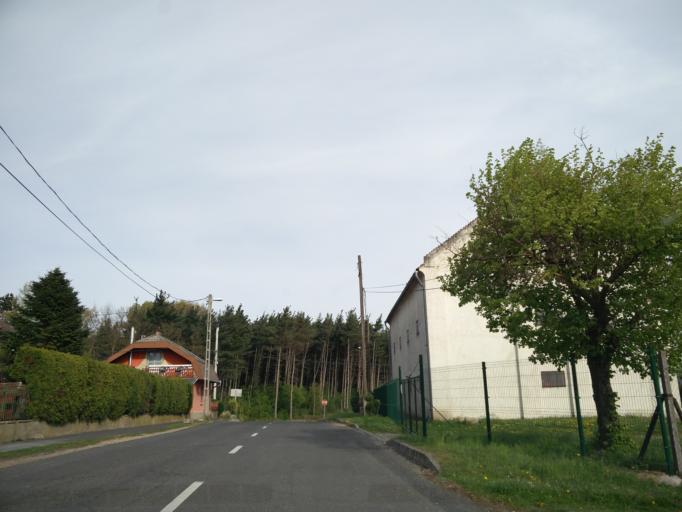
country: HU
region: Zala
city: Zalaegerszeg
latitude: 46.8640
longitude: 16.8528
